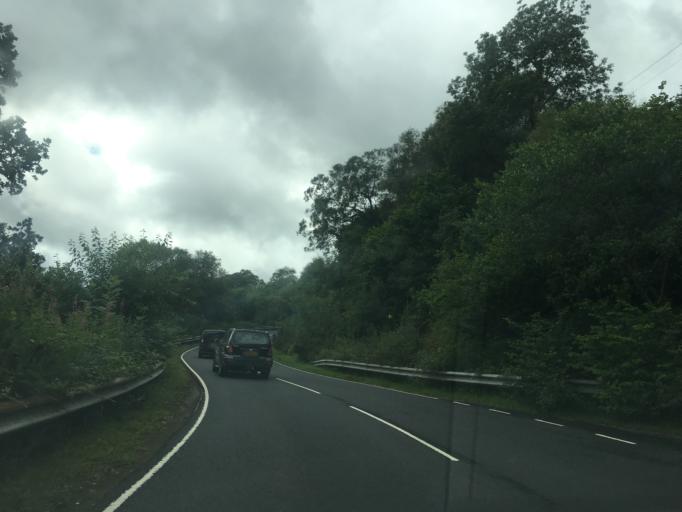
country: GB
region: Scotland
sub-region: Argyll and Bute
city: Port Bannatyne
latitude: 56.0049
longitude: -5.1296
